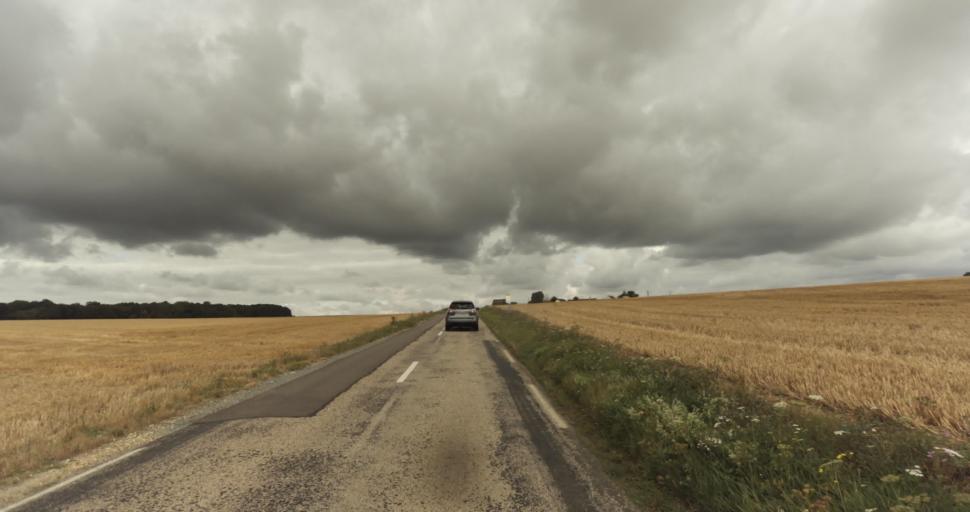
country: FR
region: Haute-Normandie
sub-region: Departement de l'Eure
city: Gravigny
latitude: 48.9976
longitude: 1.2397
